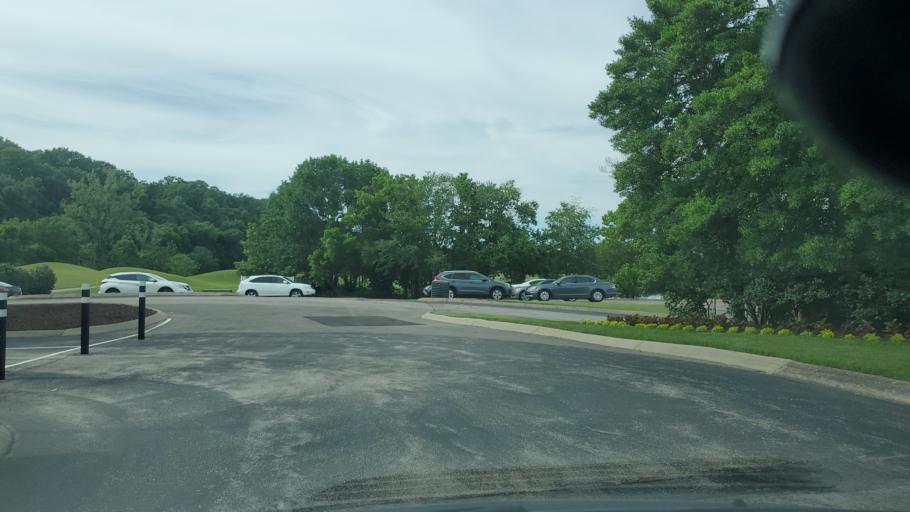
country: US
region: Tennessee
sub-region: Davidson County
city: Lakewood
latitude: 36.2206
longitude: -86.6807
